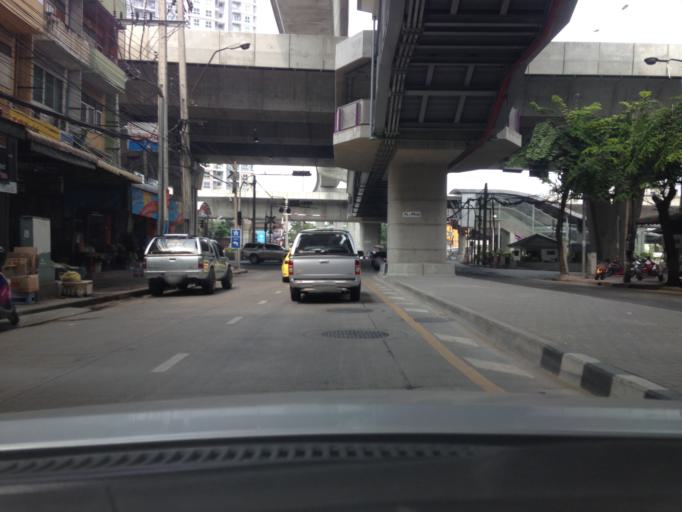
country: TH
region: Bangkok
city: Bang Sue
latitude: 13.8213
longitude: 100.5326
